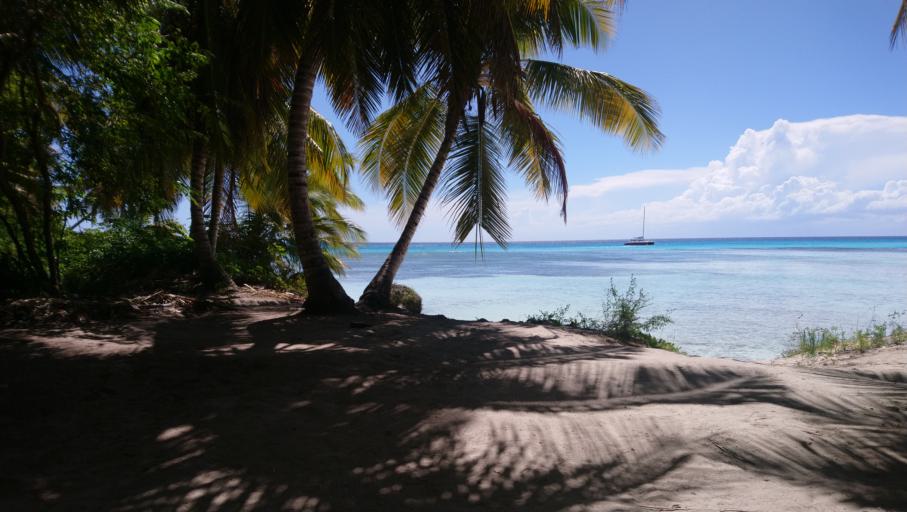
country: DO
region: La Altagracia
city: Boca de Yuma
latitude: 18.1751
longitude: -68.7842
